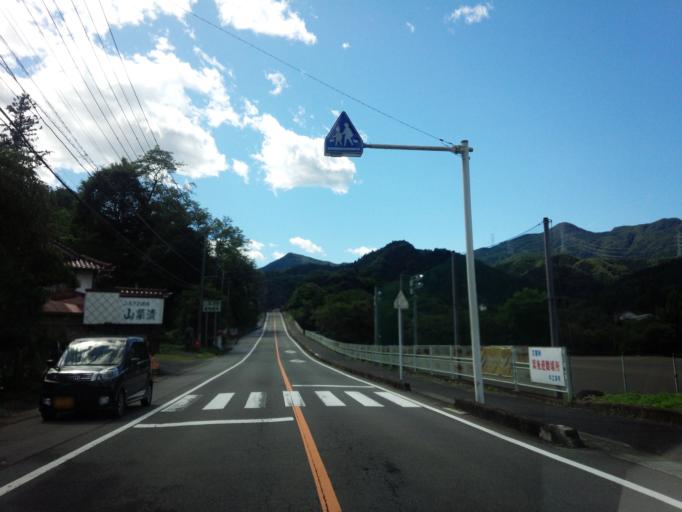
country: JP
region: Gunma
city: Nakanojomachi
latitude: 36.6145
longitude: 138.7967
